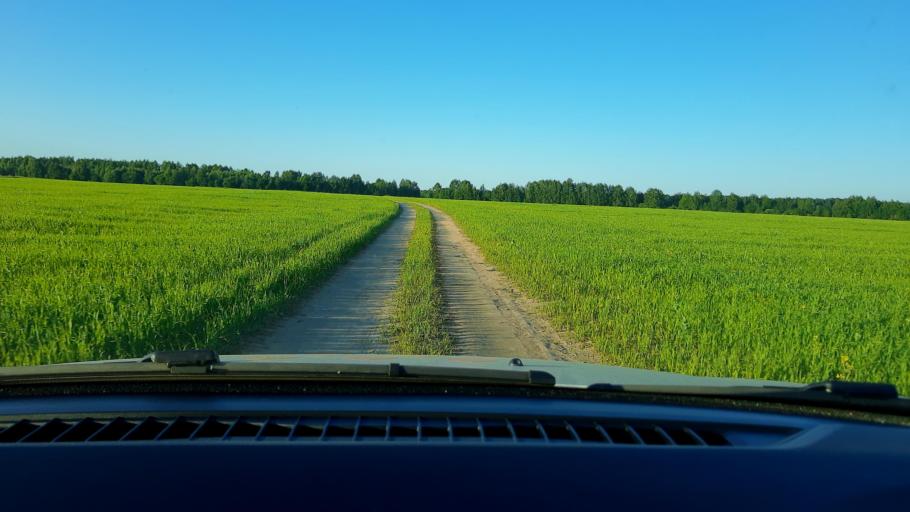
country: RU
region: Nizjnij Novgorod
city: Kstovo
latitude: 56.3031
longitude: 44.2589
